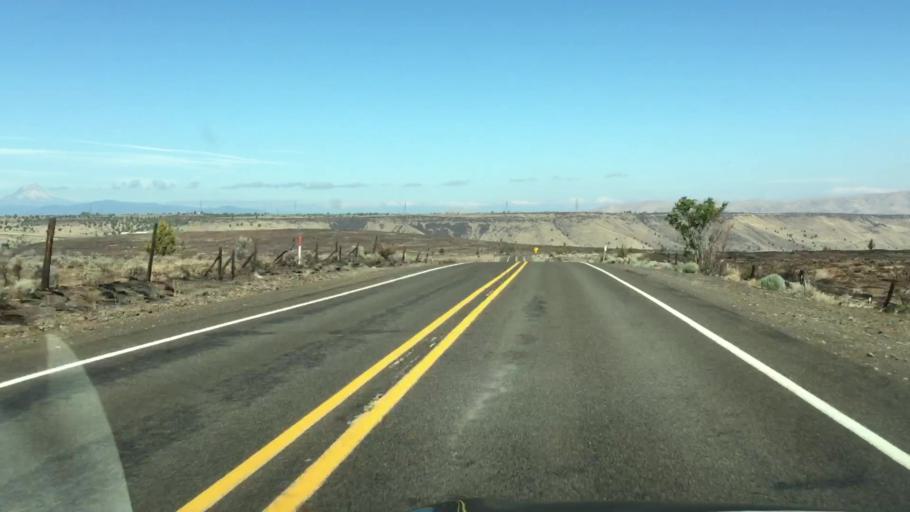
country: US
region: Oregon
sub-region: Jefferson County
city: Warm Springs
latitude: 45.1565
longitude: -121.0673
